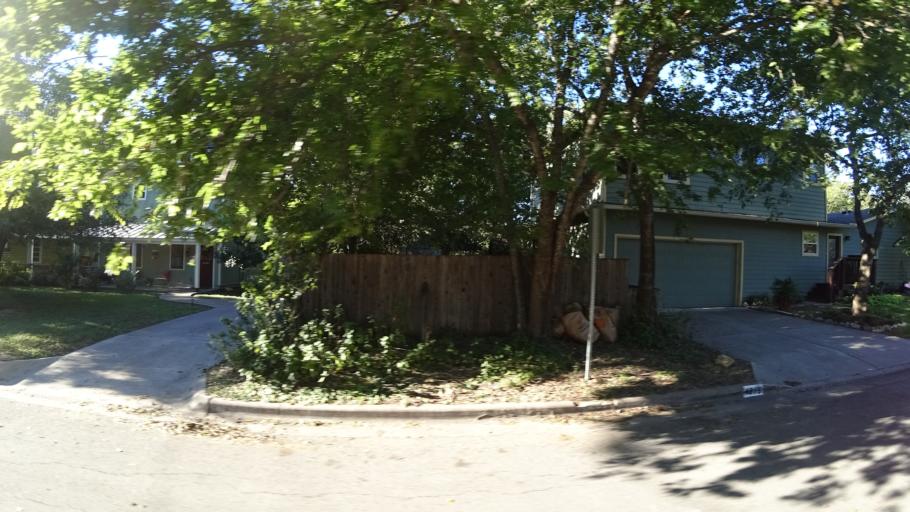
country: US
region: Texas
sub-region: Travis County
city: Austin
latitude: 30.3119
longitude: -97.7209
